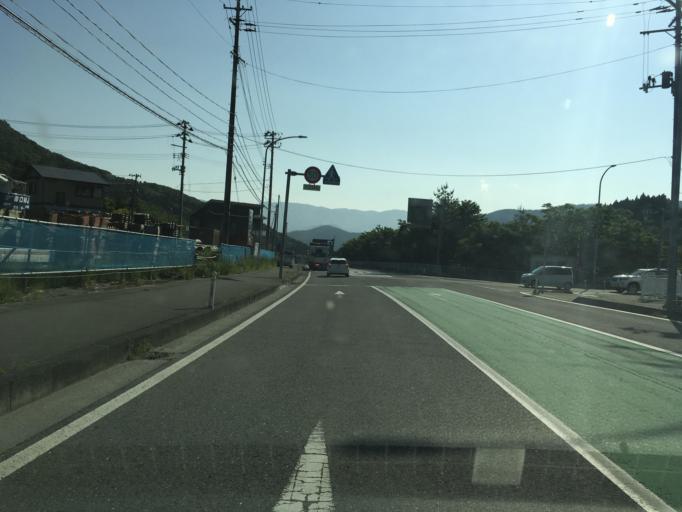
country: JP
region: Iwate
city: Ofunato
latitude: 39.1236
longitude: 141.7398
